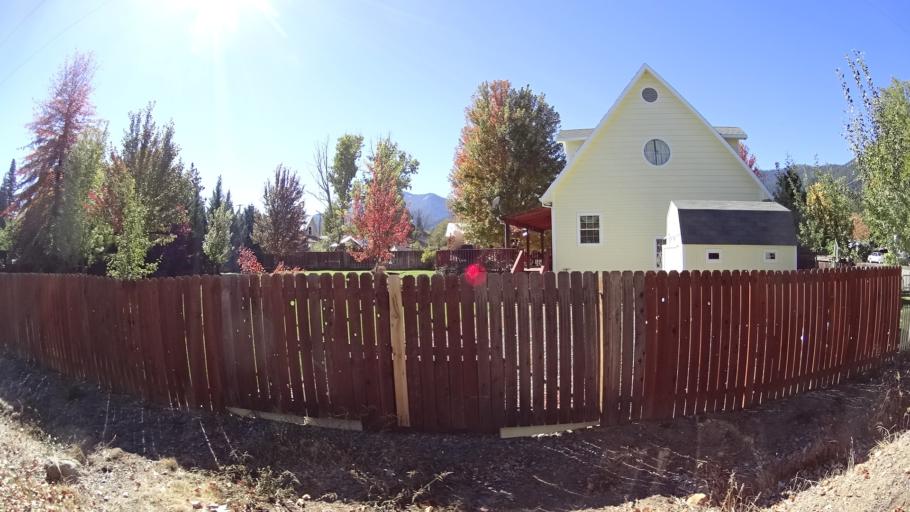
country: US
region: California
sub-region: Siskiyou County
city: Yreka
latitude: 41.4598
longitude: -122.8921
